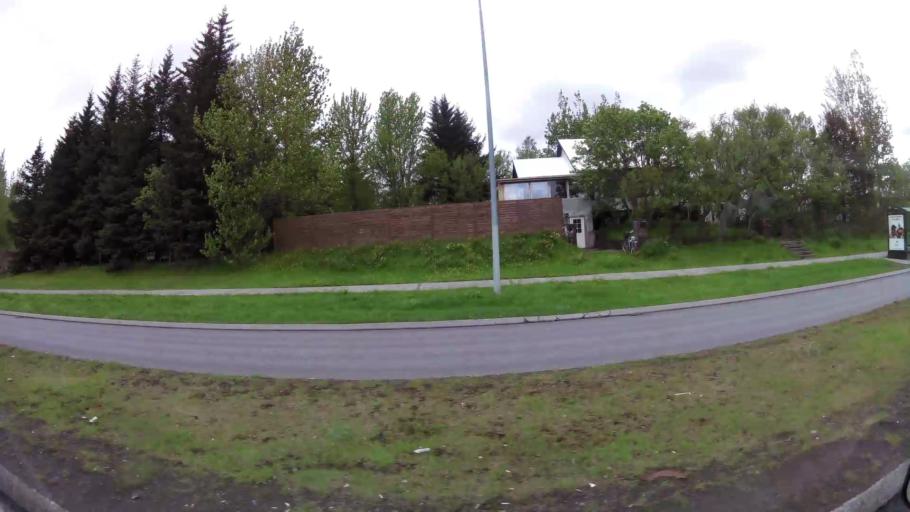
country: IS
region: Capital Region
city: Reykjavik
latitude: 64.1204
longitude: -21.8553
